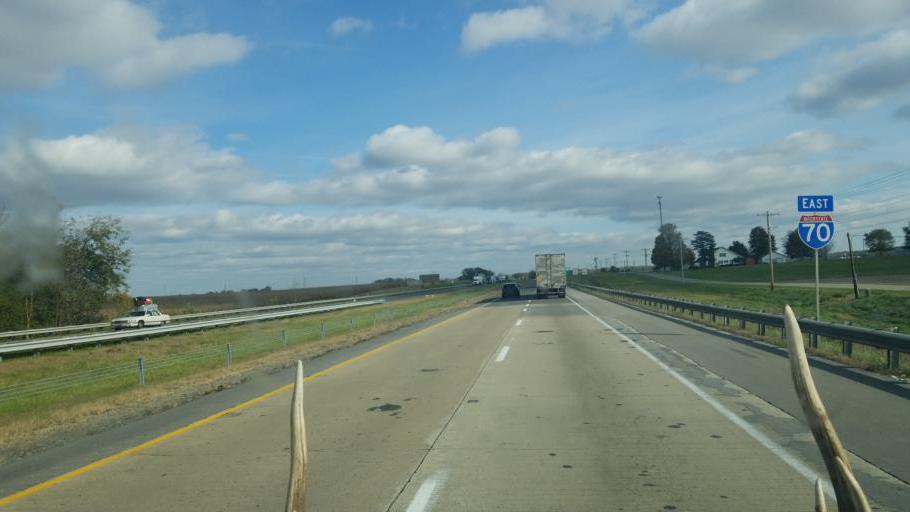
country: US
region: Indiana
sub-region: Wayne County
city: Cambridge City
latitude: 39.8527
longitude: -85.1340
